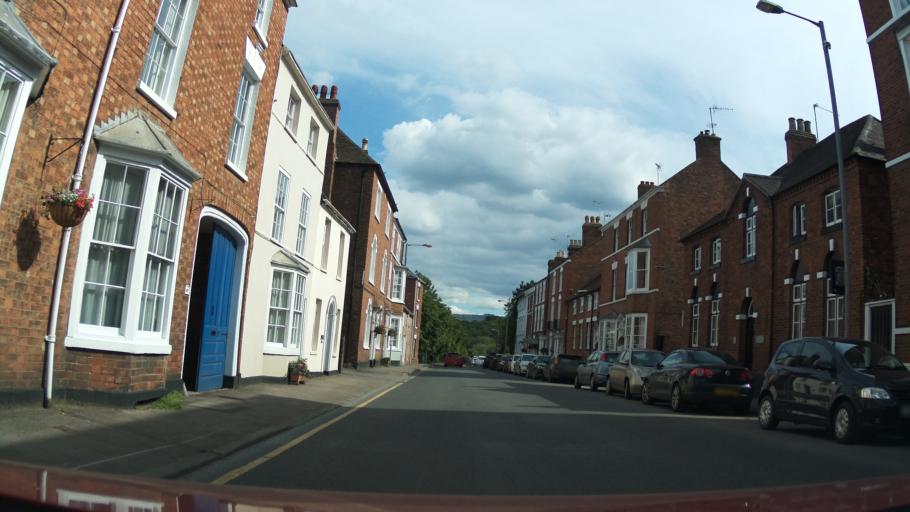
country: GB
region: England
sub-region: Worcestershire
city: Pershore
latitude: 52.1081
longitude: -2.0734
